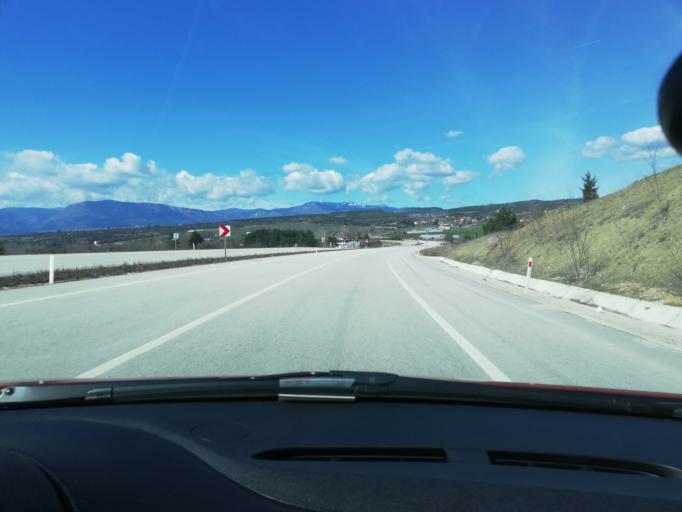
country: TR
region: Karabuk
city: Safranbolu
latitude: 41.2171
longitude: 32.7870
